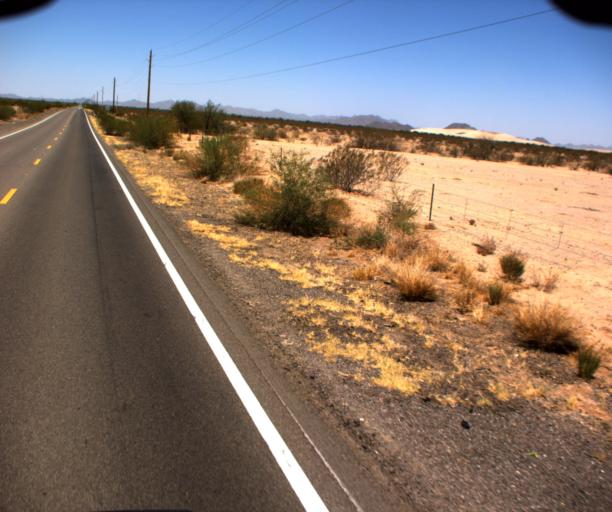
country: US
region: Arizona
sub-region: Pinal County
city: Maricopa
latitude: 33.0640
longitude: -112.2381
